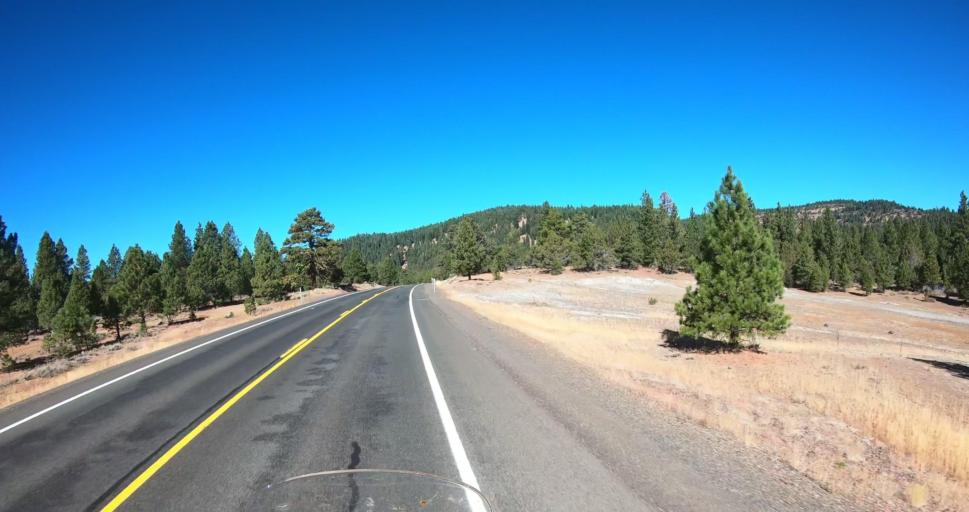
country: US
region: Oregon
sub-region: Lake County
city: Lakeview
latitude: 42.2281
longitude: -120.2568
